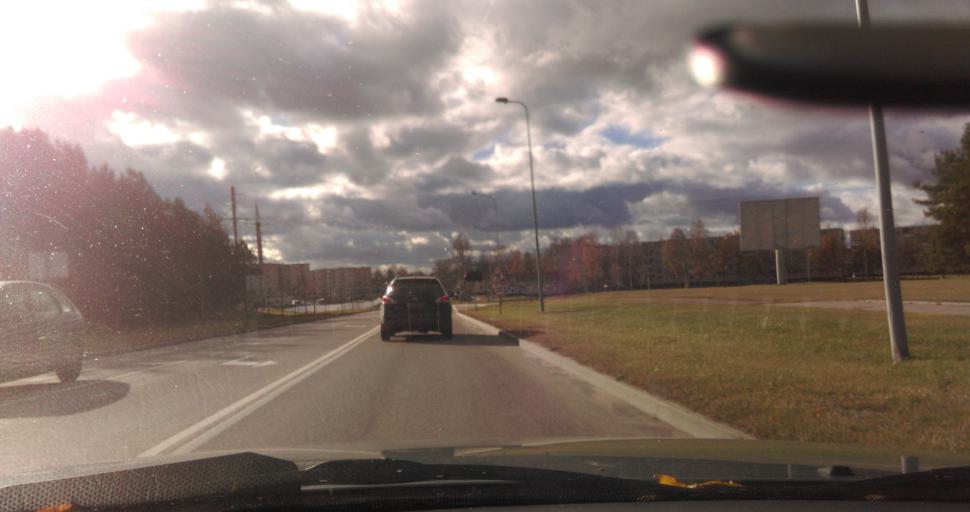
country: LT
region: Utenos apskritis
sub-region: Utena
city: Utena
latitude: 55.5042
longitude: 25.6217
